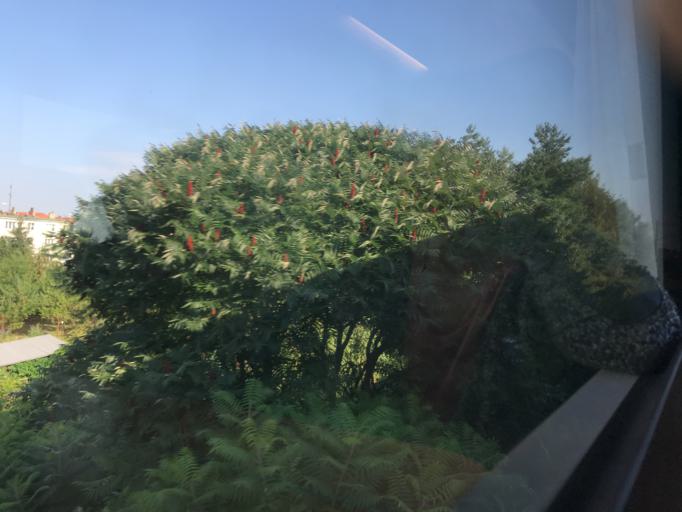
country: CZ
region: Jihocesky
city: Sobeslav
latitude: 49.2588
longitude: 14.7265
